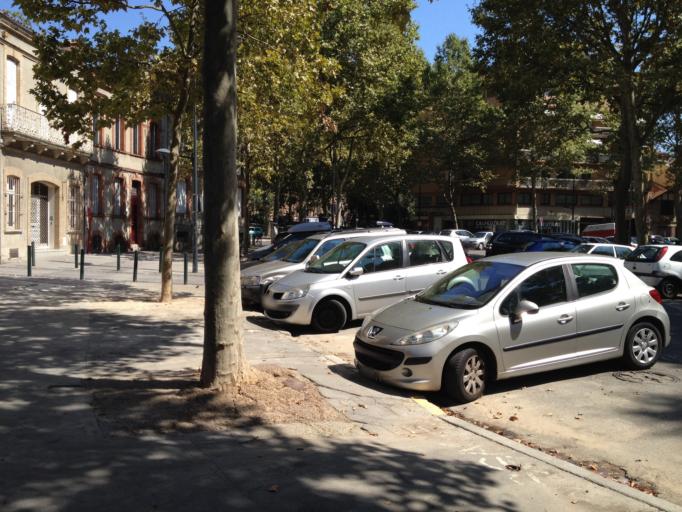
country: FR
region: Midi-Pyrenees
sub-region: Departement de la Haute-Garonne
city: Toulouse
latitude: 43.6040
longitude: 1.4557
